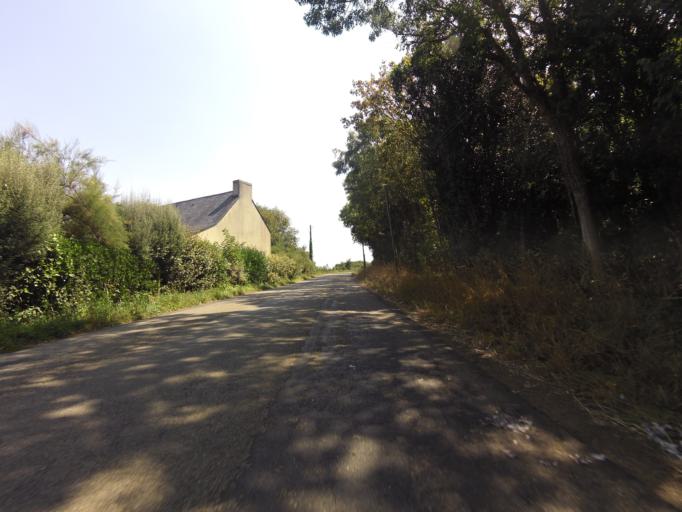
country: FR
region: Brittany
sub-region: Departement du Finistere
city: Pouldreuzic
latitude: 47.9123
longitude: -4.3438
